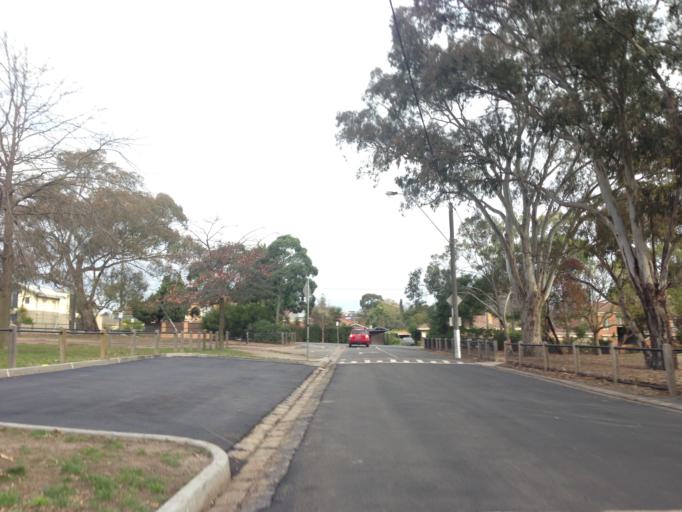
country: AU
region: Victoria
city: Balwyn
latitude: -37.8017
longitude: 145.0749
